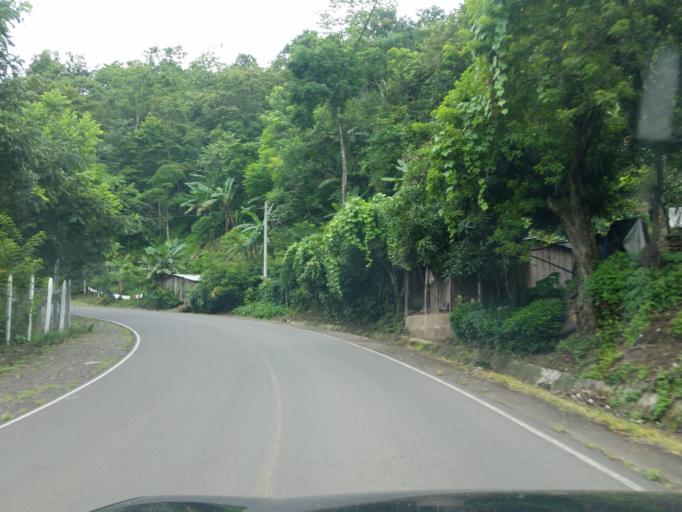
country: NI
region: Matagalpa
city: San Ramon
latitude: 12.9963
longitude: -85.8190
